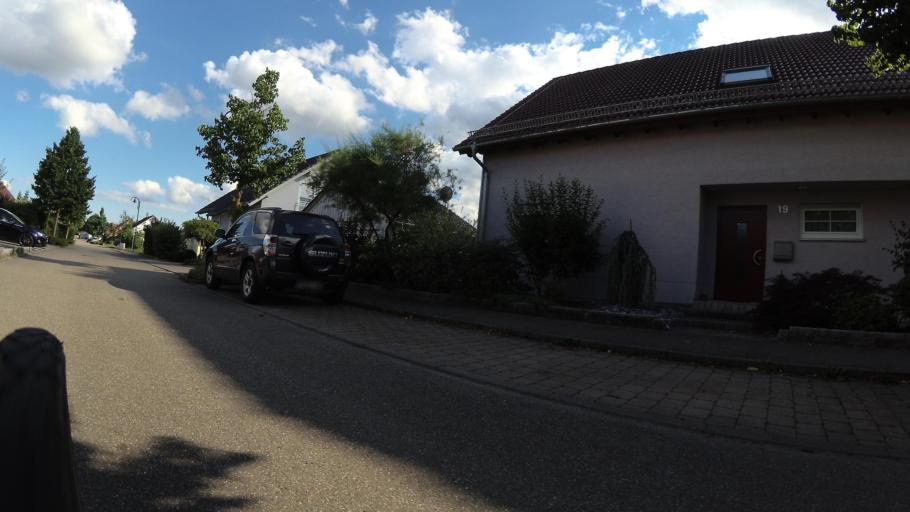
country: DE
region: Baden-Wuerttemberg
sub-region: Regierungsbezirk Stuttgart
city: Neuenstadt am Kocher
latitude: 49.2488
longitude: 9.3088
